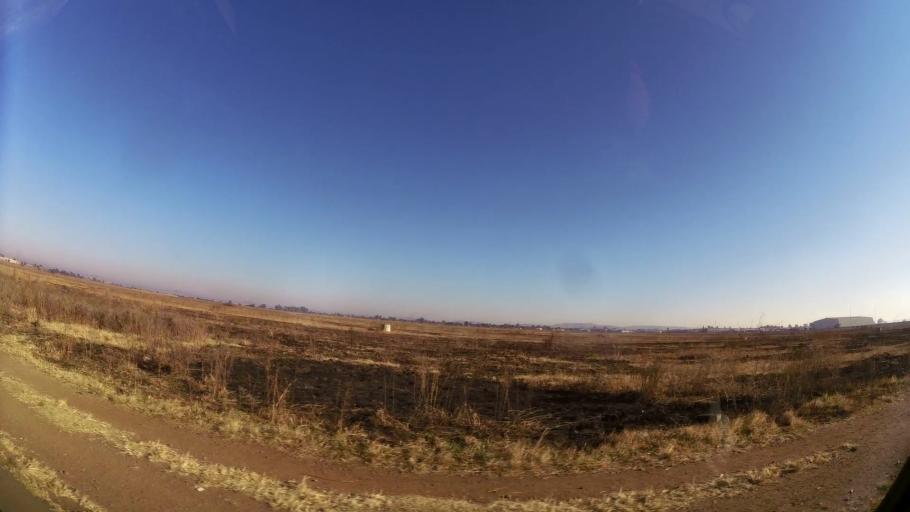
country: ZA
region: Gauteng
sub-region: Ekurhuleni Metropolitan Municipality
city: Germiston
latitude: -26.3367
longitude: 28.1349
